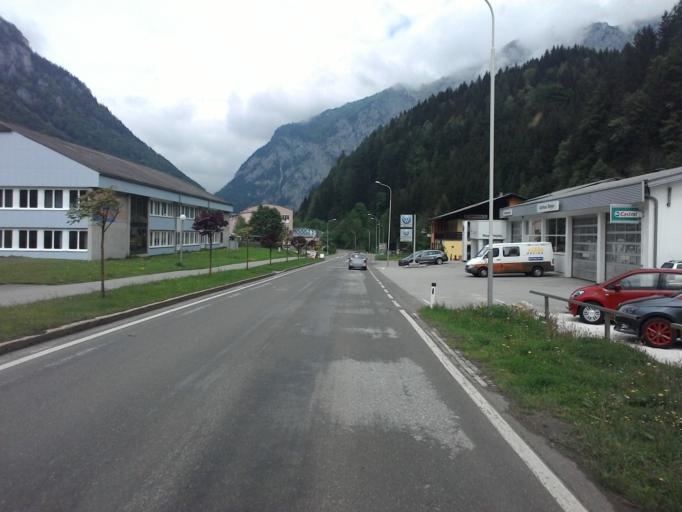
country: AT
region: Styria
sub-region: Politischer Bezirk Leoben
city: Eisenerz
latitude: 47.5593
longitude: 14.8670
